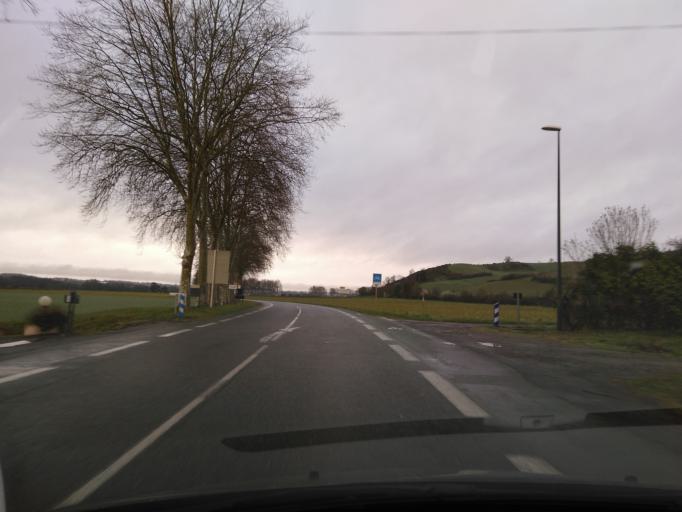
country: FR
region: Midi-Pyrenees
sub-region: Departement de la Haute-Garonne
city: Montesquieu-Volvestre
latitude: 43.2195
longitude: 1.2183
